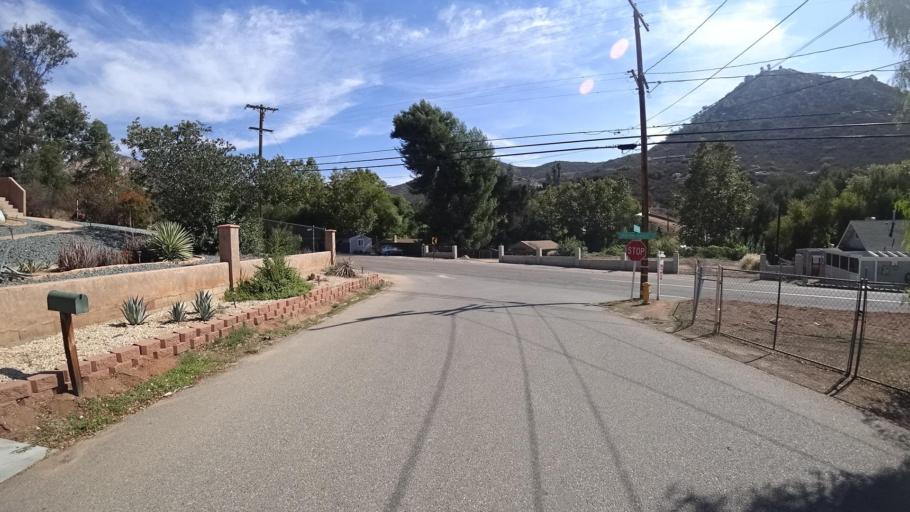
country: US
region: California
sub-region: San Diego County
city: Harbison Canyon
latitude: 32.8188
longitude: -116.8314
